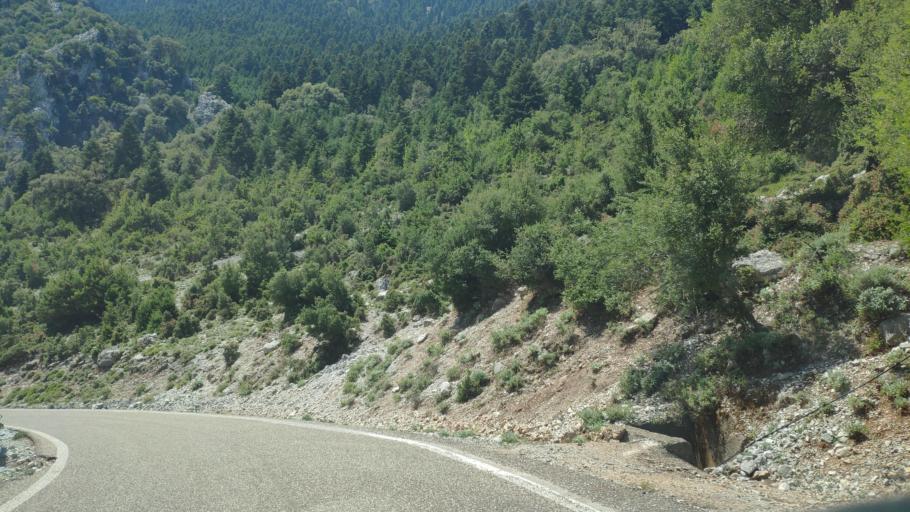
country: GR
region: West Greece
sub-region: Nomos Aitolias kai Akarnanias
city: Krikellos
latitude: 39.0086
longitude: 21.3603
